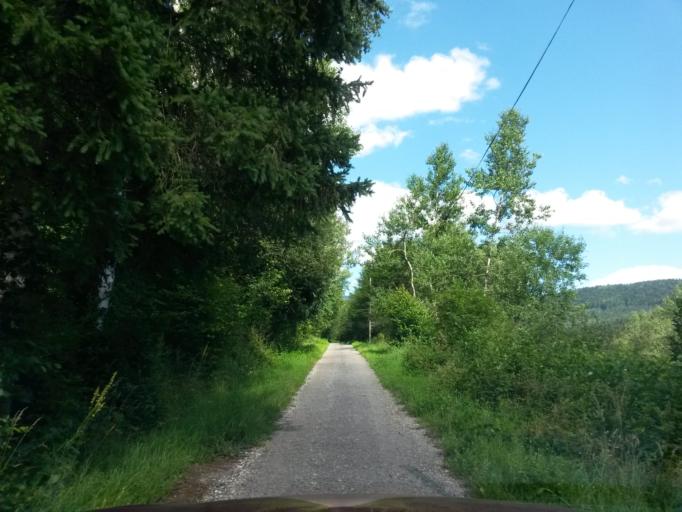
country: SK
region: Kosicky
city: Medzev
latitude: 48.7939
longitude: 20.7570
